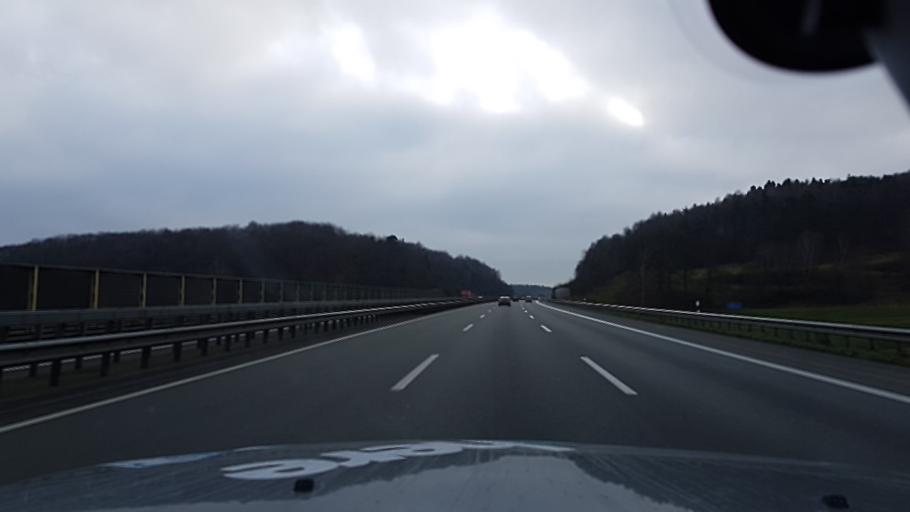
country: DE
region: Lower Saxony
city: Wallenhorst
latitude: 52.3769
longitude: 8.0438
